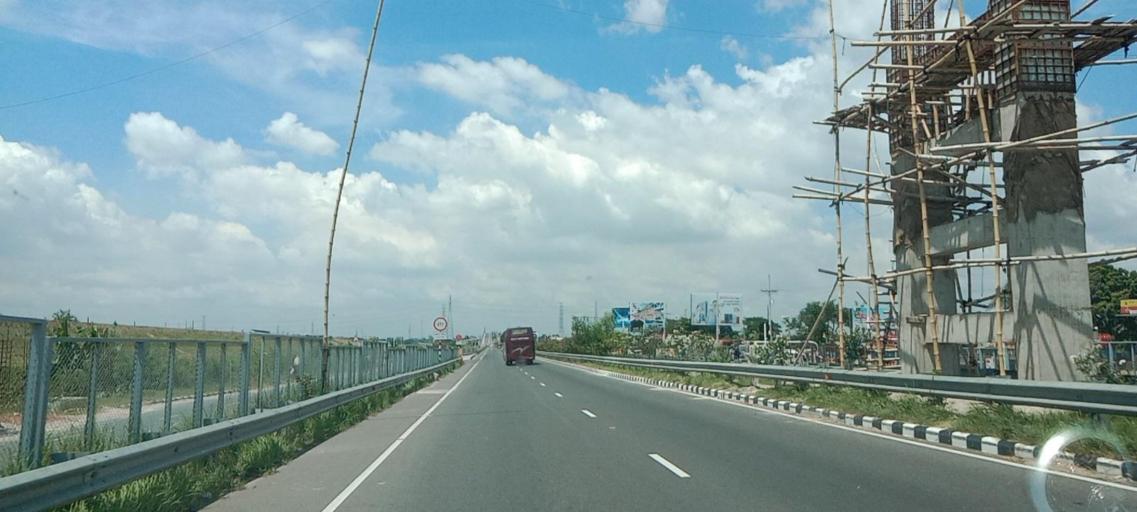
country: BD
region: Dhaka
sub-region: Dhaka
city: Dhaka
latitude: 23.6168
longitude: 90.3329
